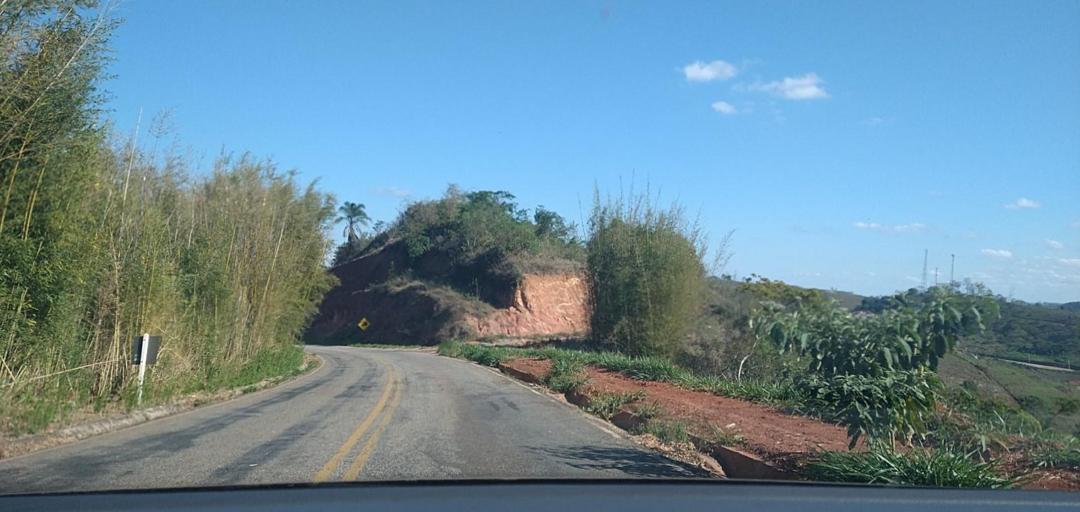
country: BR
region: Minas Gerais
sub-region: Ponte Nova
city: Ponte Nova
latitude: -20.2363
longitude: -42.8998
